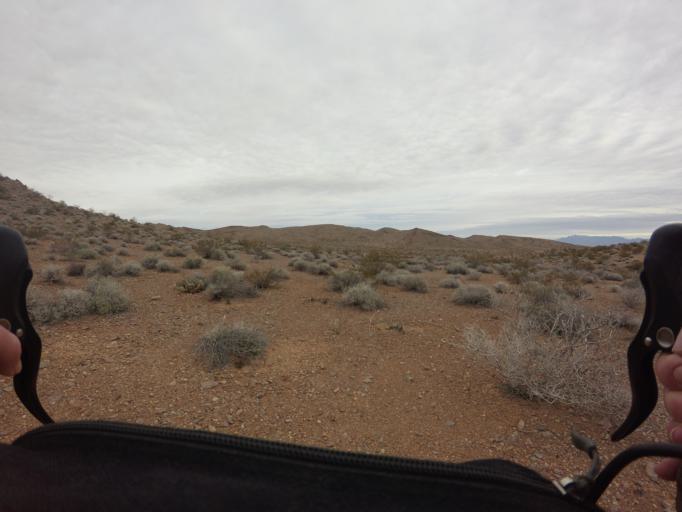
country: US
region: Nevada
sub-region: Clark County
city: Boulder City
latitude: 36.2256
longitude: -114.6200
